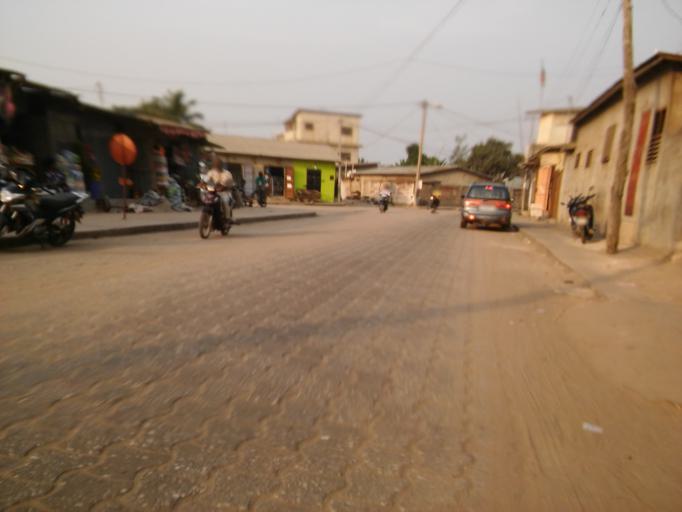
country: BJ
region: Atlantique
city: Abomey-Calavi
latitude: 6.3957
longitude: 2.3460
